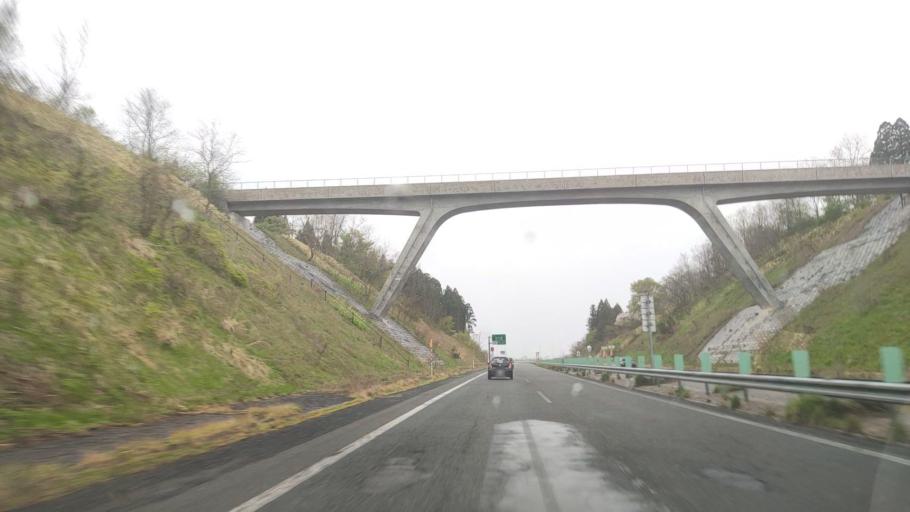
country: JP
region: Akita
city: Noshiromachi
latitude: 40.1844
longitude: 140.0882
